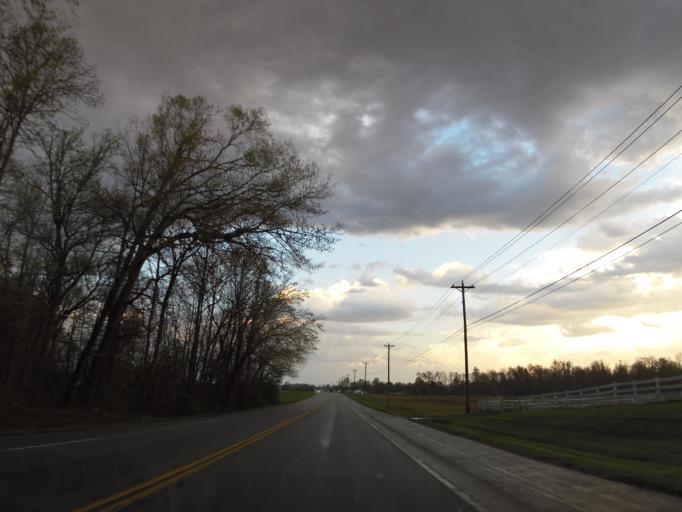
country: US
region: Tennessee
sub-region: DeKalb County
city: Smithville
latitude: 35.9728
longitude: -85.8064
